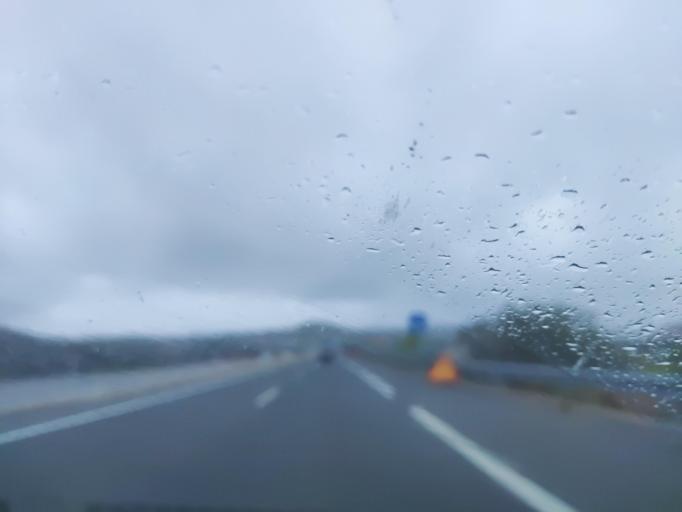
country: ES
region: Castille-La Mancha
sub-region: Province of Toledo
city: Toledo
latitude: 39.8685
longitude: -4.0849
